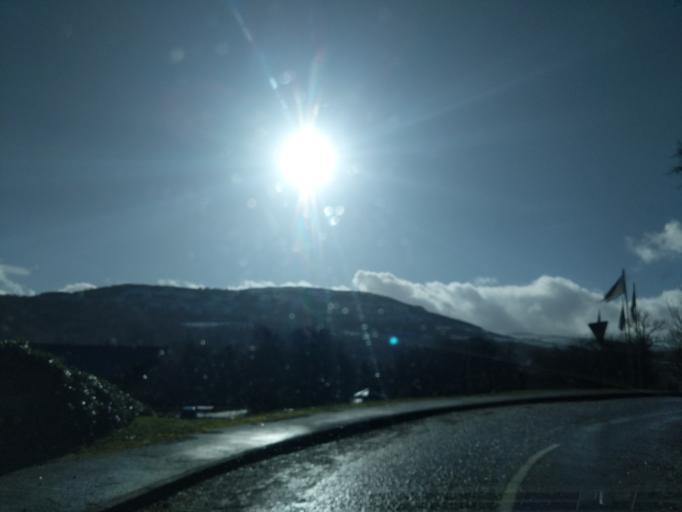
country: GB
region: Scotland
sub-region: Perth and Kinross
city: Aberfeldy
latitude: 56.5880
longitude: -4.0033
